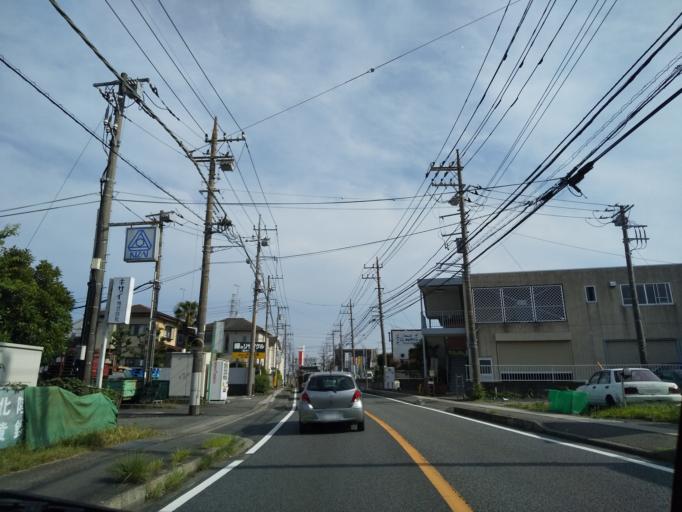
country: JP
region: Kanagawa
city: Zama
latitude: 35.4935
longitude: 139.3394
